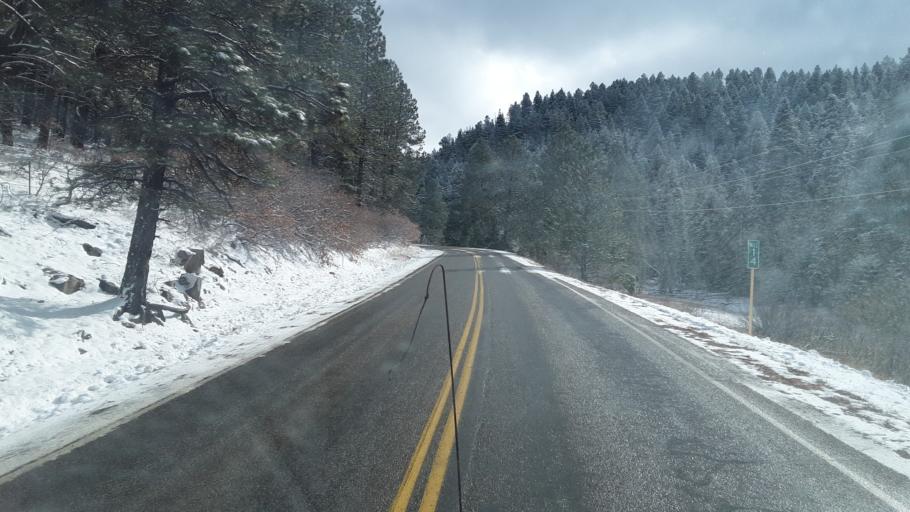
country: US
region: Colorado
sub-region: La Plata County
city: Bayfield
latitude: 37.3584
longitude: -107.6689
